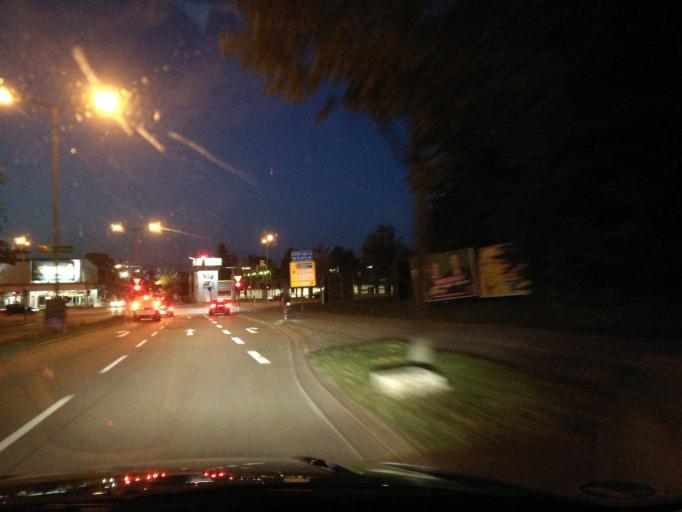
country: DE
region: Bavaria
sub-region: Upper Palatinate
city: Pentling
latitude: 49.0094
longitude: 12.0637
